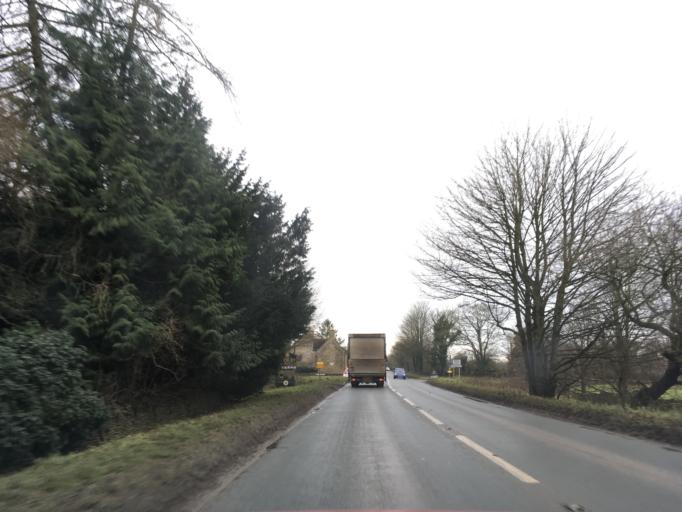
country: GB
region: England
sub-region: Gloucestershire
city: Tetbury
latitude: 51.6479
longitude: -2.1424
